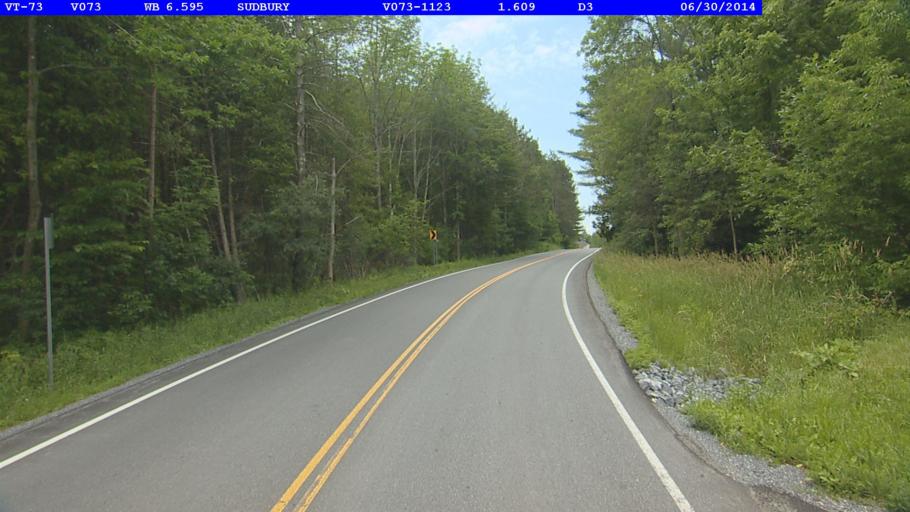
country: US
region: Vermont
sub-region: Rutland County
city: Brandon
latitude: 43.8205
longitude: -73.1696
